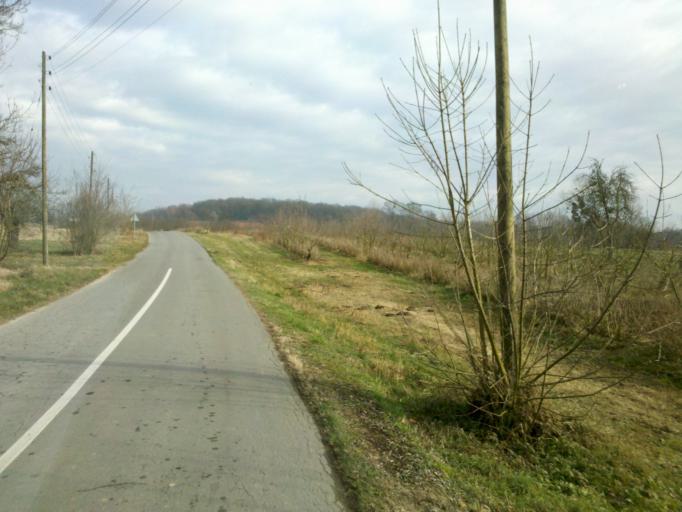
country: HR
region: Koprivnicko-Krizevacka
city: Molve
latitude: 46.1047
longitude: 17.0654
